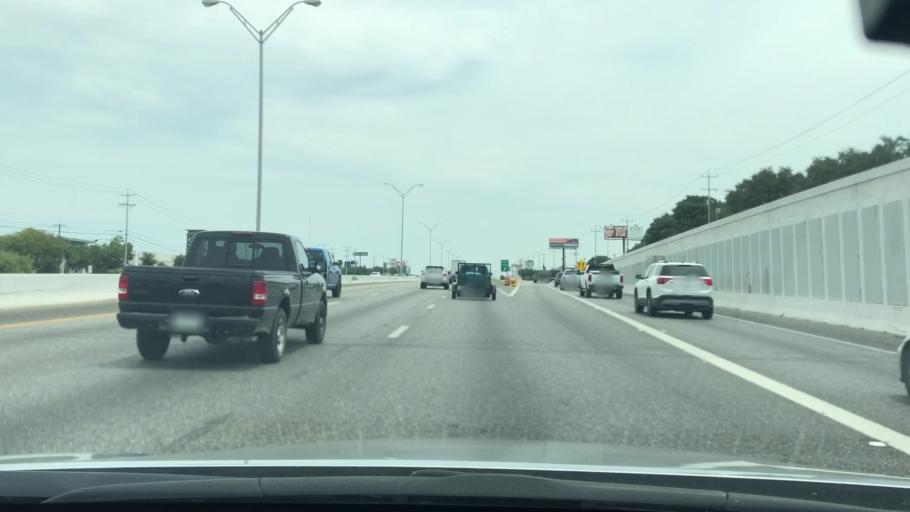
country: US
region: Texas
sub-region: Bexar County
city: Selma
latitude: 29.5950
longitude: -98.2883
